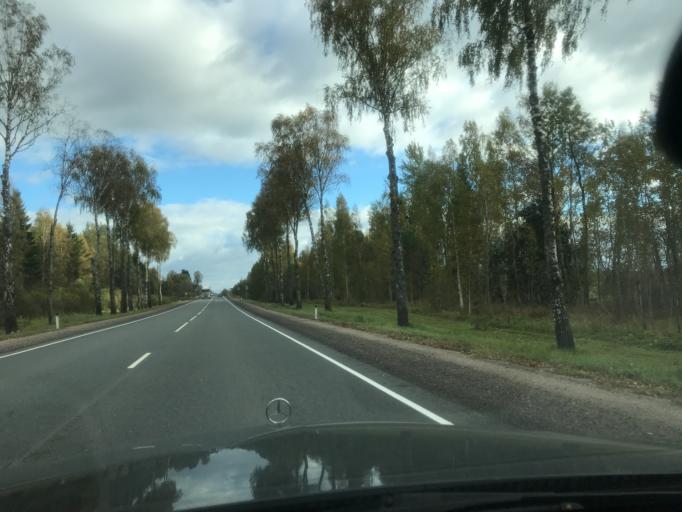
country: RU
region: Pskov
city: Opochka
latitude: 56.6758
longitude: 28.7187
